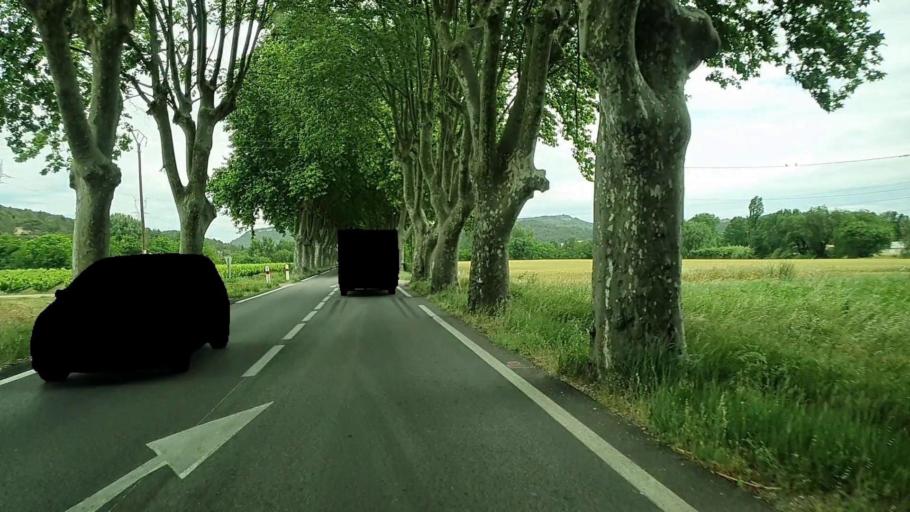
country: FR
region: Languedoc-Roussillon
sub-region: Departement du Gard
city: Connaux
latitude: 44.1000
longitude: 4.6038
